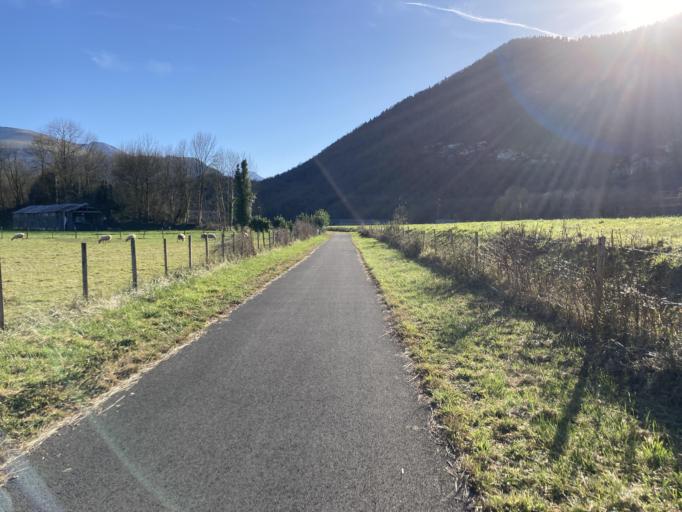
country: FR
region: Aquitaine
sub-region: Departement des Pyrenees-Atlantiques
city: Louvie-Juzon
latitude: 43.0959
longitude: -0.4326
